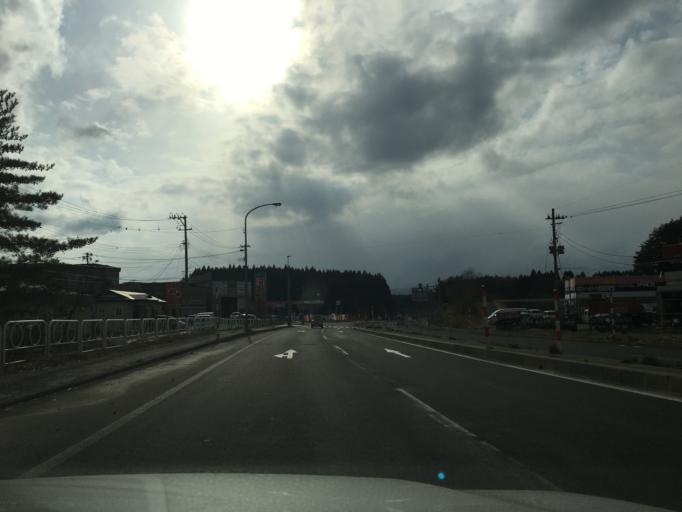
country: JP
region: Aomori
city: Aomori Shi
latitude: 40.8333
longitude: 140.6703
